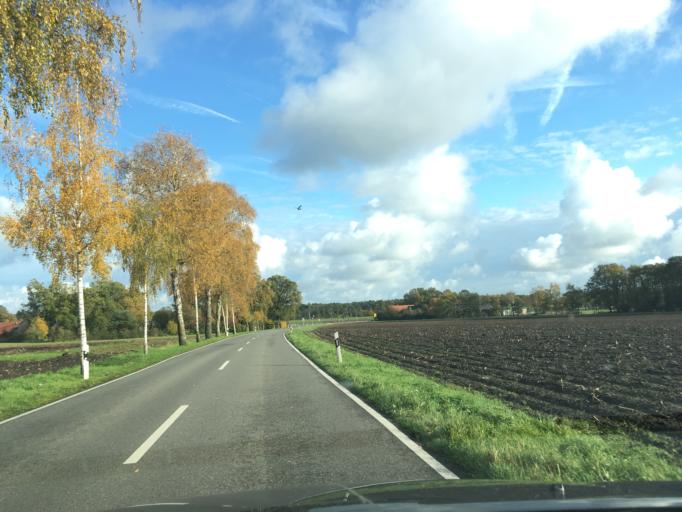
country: DE
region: North Rhine-Westphalia
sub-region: Regierungsbezirk Munster
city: Vreden
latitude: 52.0993
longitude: 6.8790
